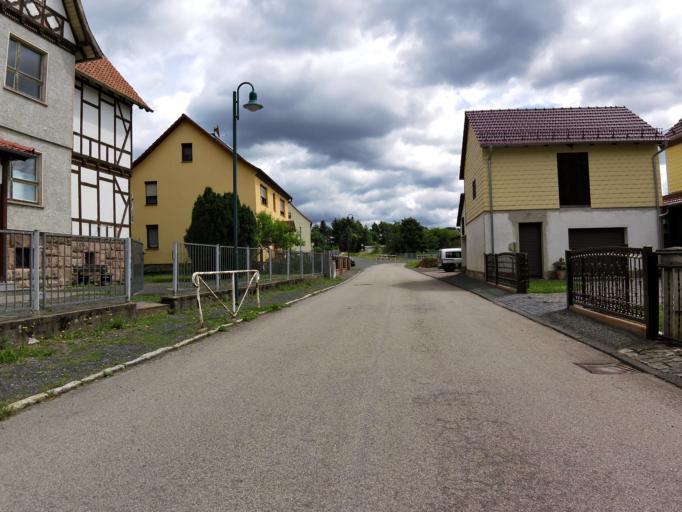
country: DE
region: Thuringia
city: Fambach
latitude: 50.7181
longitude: 10.4015
